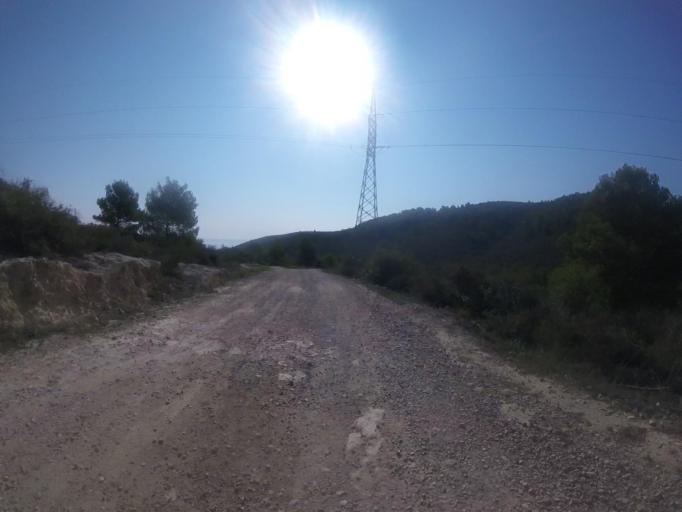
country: ES
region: Valencia
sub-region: Provincia de Castello
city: Peniscola
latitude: 40.3305
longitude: 0.3591
